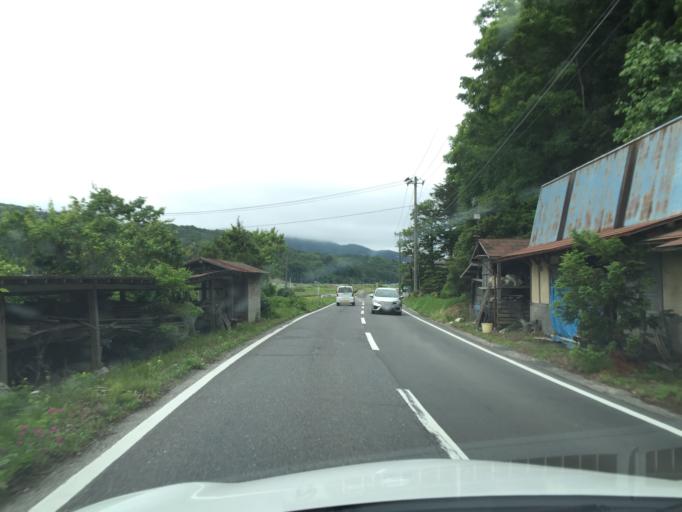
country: JP
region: Fukushima
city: Funehikimachi-funehiki
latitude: 37.3470
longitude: 140.6499
